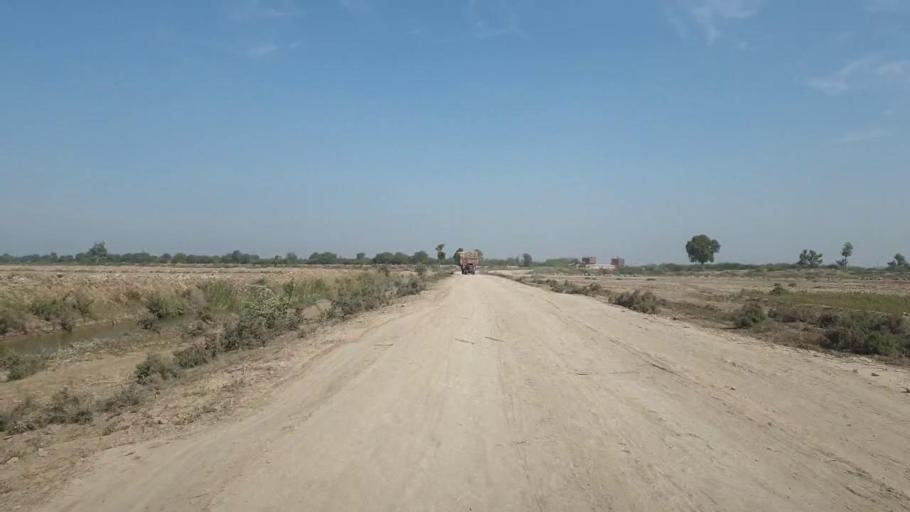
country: PK
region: Sindh
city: Samaro
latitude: 25.3182
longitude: 69.2324
